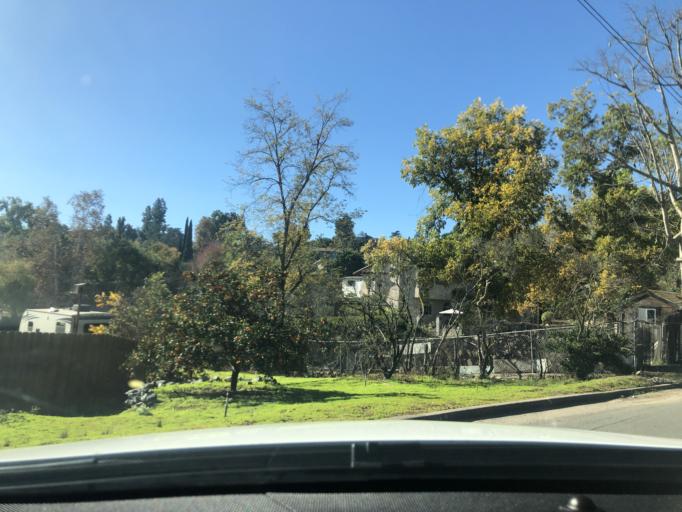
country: US
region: California
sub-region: San Diego County
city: Casa de Oro-Mount Helix
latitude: 32.7732
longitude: -116.9454
